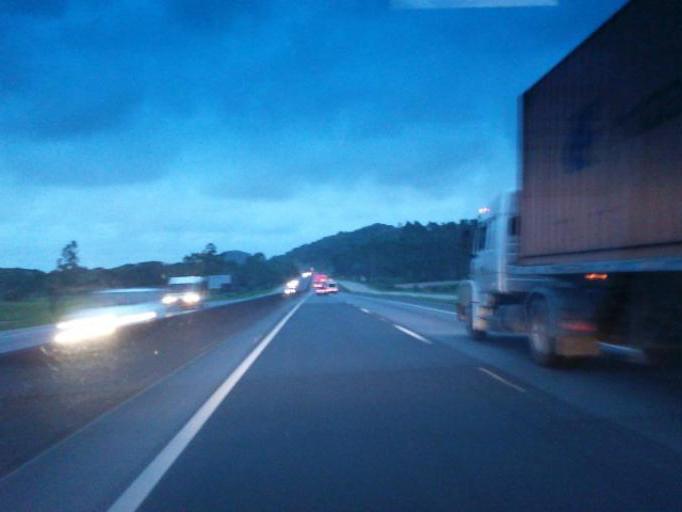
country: BR
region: Santa Catarina
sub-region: Barra Velha
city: Barra Velha
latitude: -26.6888
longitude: -48.6962
